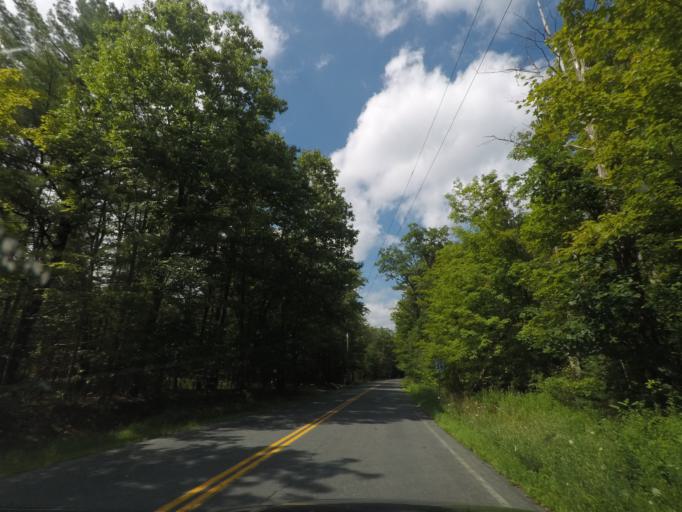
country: US
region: New York
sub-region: Rensselaer County
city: Averill Park
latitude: 42.6054
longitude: -73.5537
